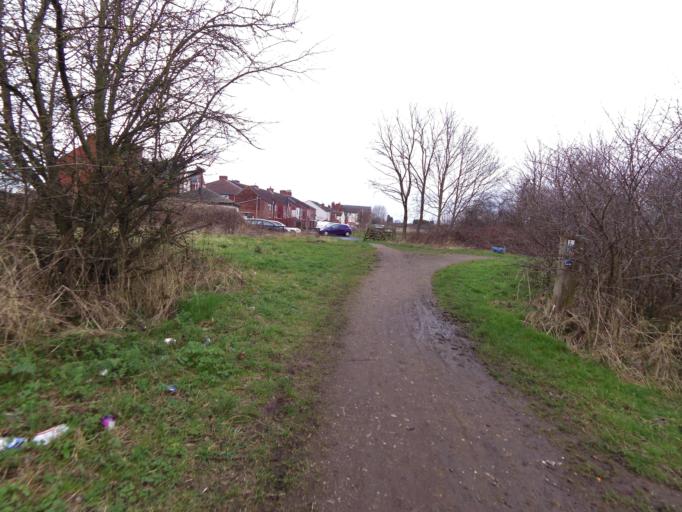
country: GB
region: England
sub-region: Doncaster
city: Bentley
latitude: 53.5622
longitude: -1.1523
